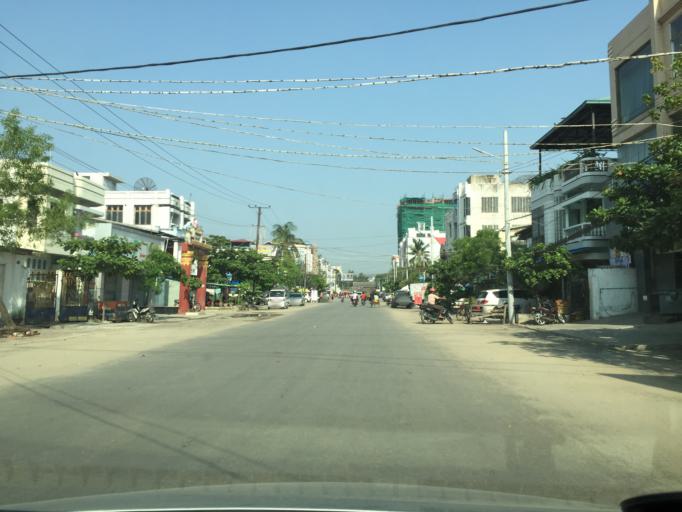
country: MM
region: Mandalay
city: Mandalay
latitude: 21.9737
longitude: 96.0897
